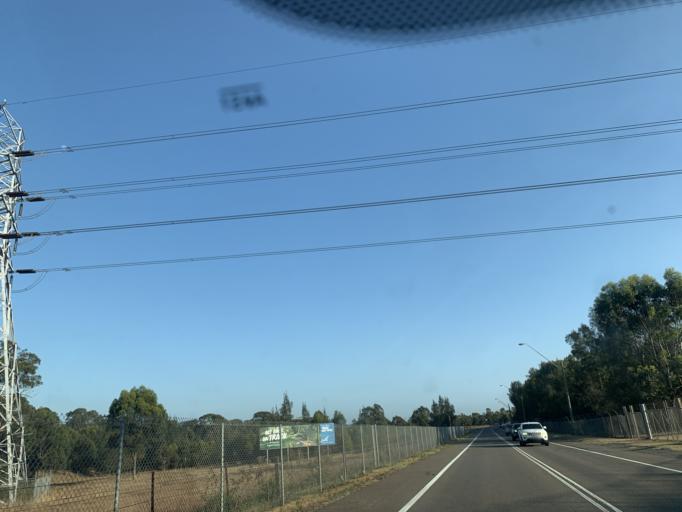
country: AU
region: New South Wales
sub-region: Blacktown
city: Doonside
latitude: -33.8055
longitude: 150.8642
